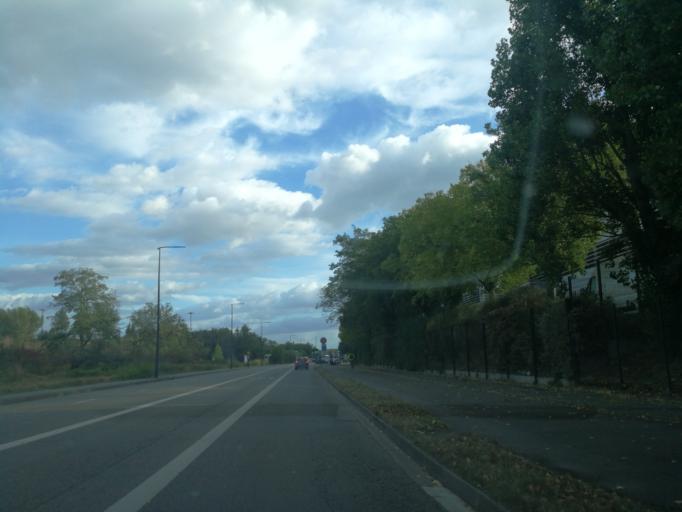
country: FR
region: Midi-Pyrenees
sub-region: Departement de la Haute-Garonne
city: Balma
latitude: 43.6304
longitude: 1.4757
